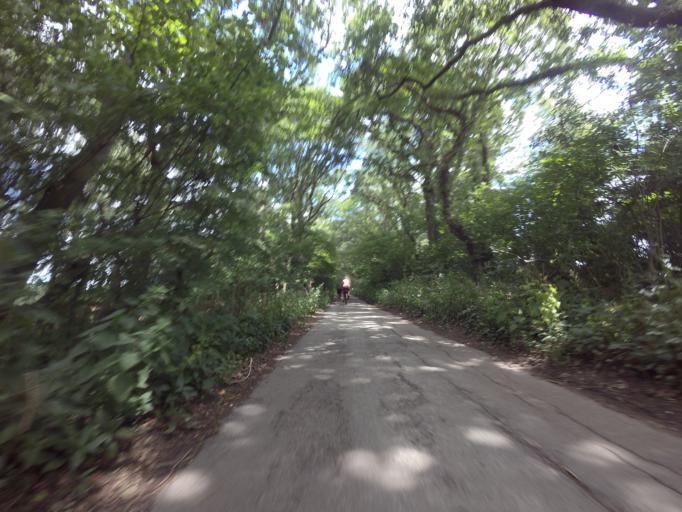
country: GB
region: England
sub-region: East Sussex
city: Hailsham
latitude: 50.8361
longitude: 0.2135
